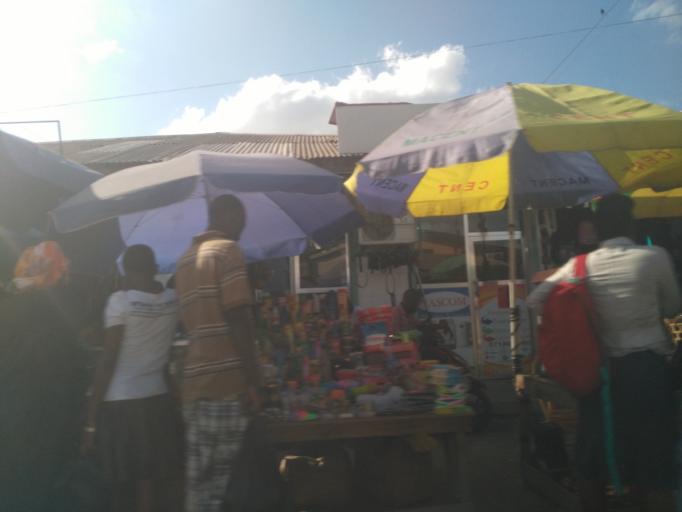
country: TZ
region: Dar es Salaam
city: Dar es Salaam
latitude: -6.8669
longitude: 39.2619
